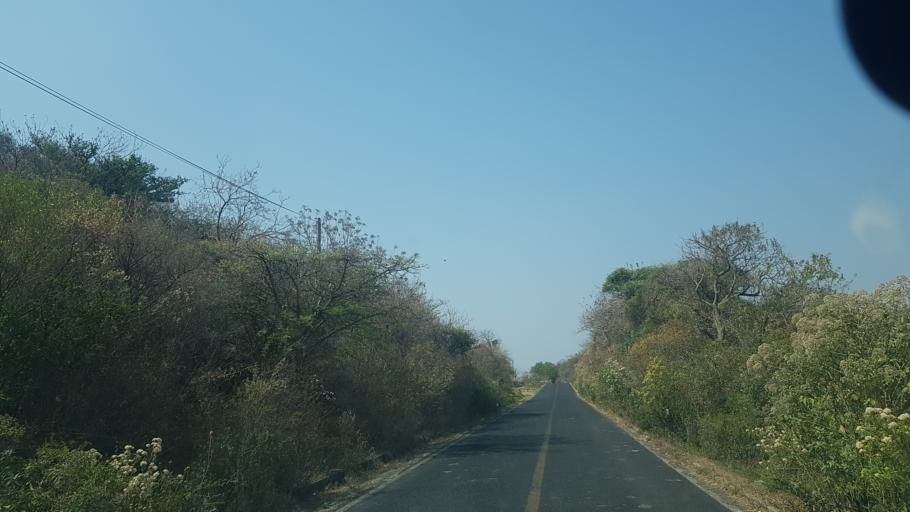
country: MX
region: Morelos
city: Tlacotepec
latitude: 18.8275
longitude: -98.7398
